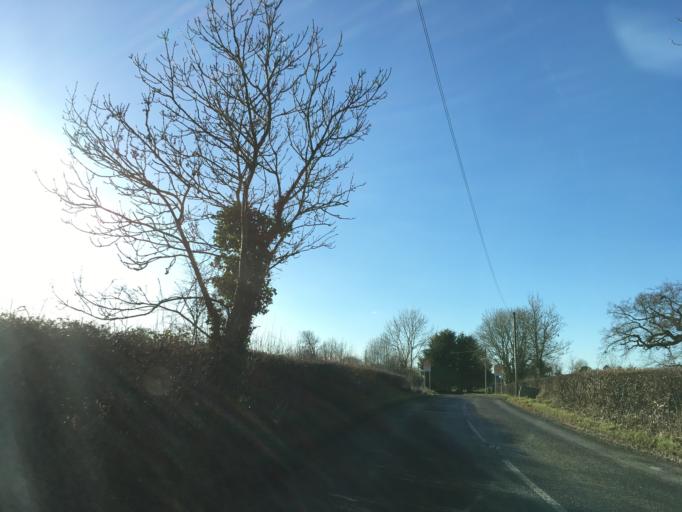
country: GB
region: England
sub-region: Wiltshire
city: Nettleton
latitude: 51.5286
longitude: -2.2716
